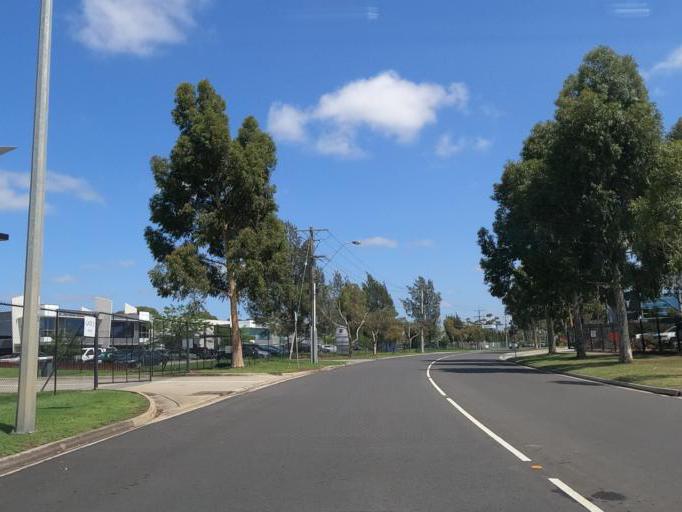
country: AU
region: Victoria
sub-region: Hume
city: Gladstone Park
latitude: -37.6834
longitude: 144.8764
